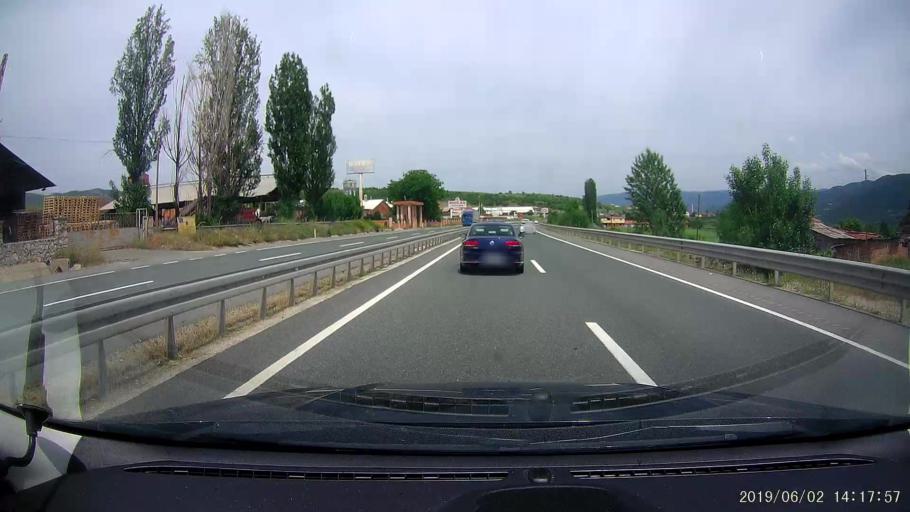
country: TR
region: Kastamonu
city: Tosya
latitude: 40.9570
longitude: 33.9437
